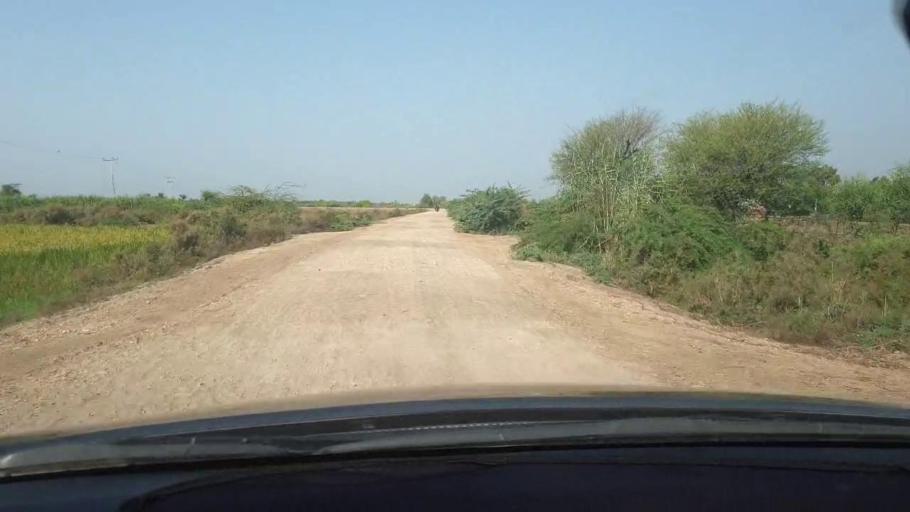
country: PK
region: Sindh
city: Tando Bago
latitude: 24.6800
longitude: 69.1298
